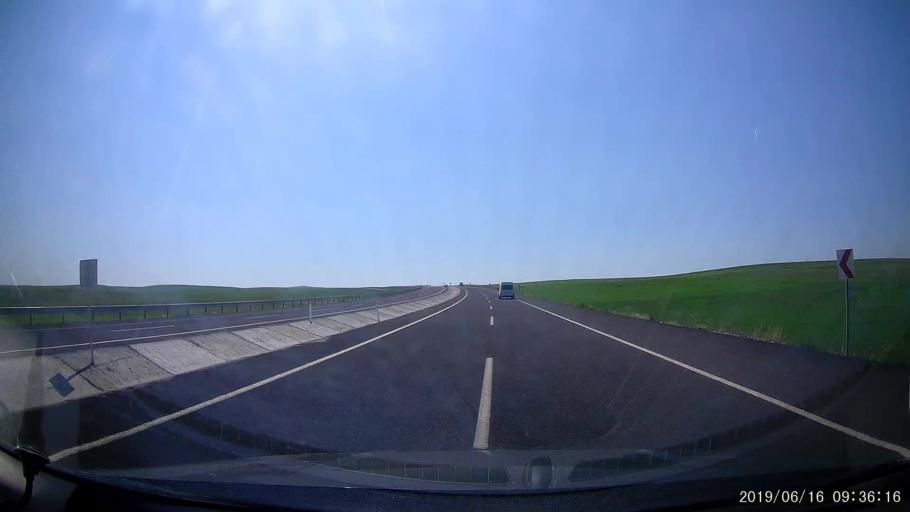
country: TR
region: Kars
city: Kars
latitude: 40.5597
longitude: 43.1692
